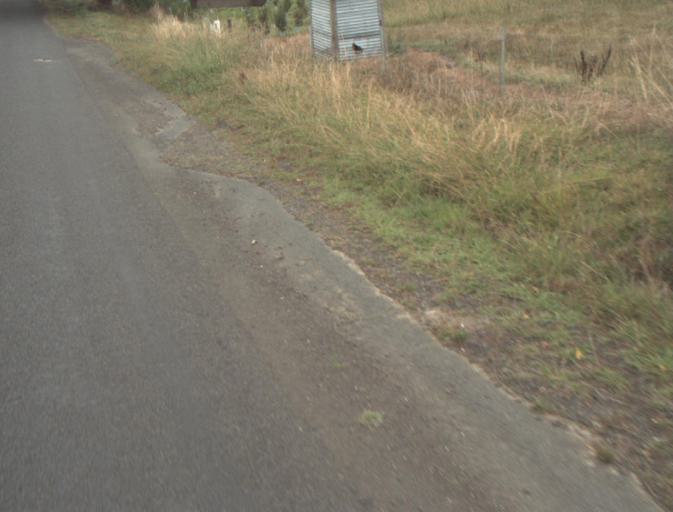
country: AU
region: Tasmania
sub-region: Northern Midlands
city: Perth
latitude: -41.5066
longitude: 147.2064
